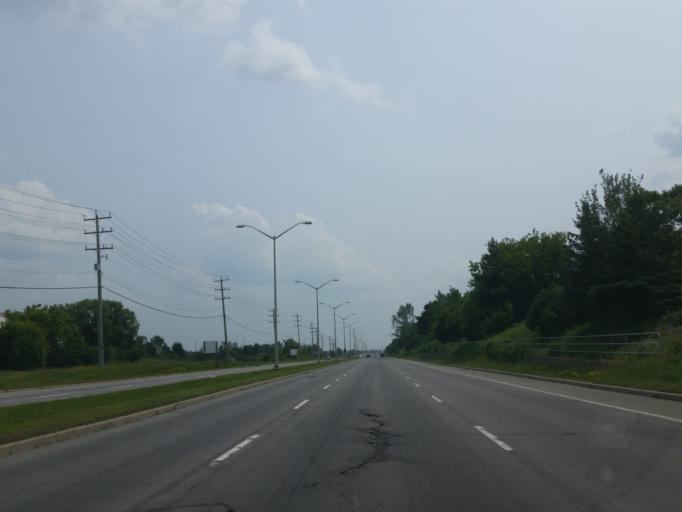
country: CA
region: Ontario
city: Bells Corners
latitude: 45.3298
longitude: -75.8917
